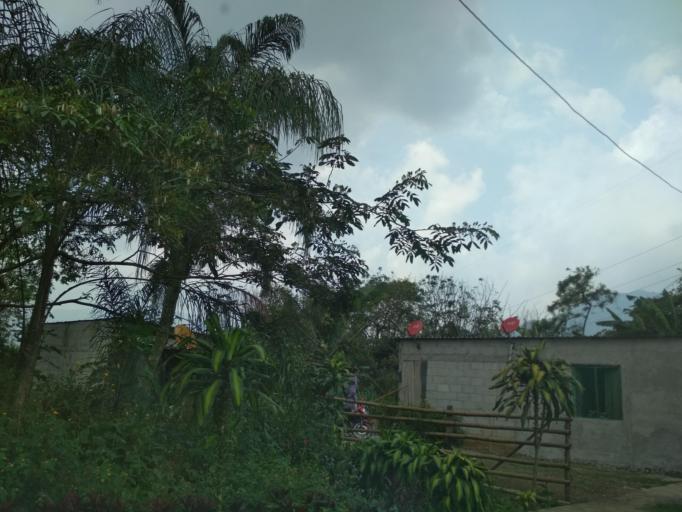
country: MX
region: Veracruz
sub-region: Cordoba
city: San Jose de Tapia
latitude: 18.8365
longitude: -96.9800
